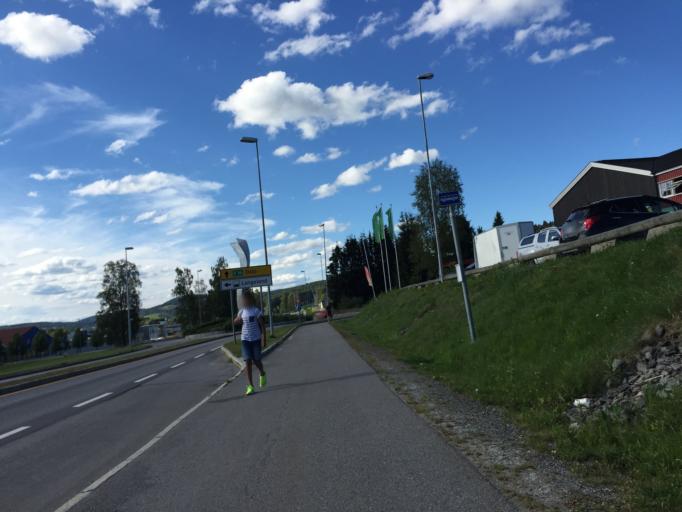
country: NO
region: Hedmark
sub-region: Kongsvinger
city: Kongsvinger
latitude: 60.2014
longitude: 11.9793
